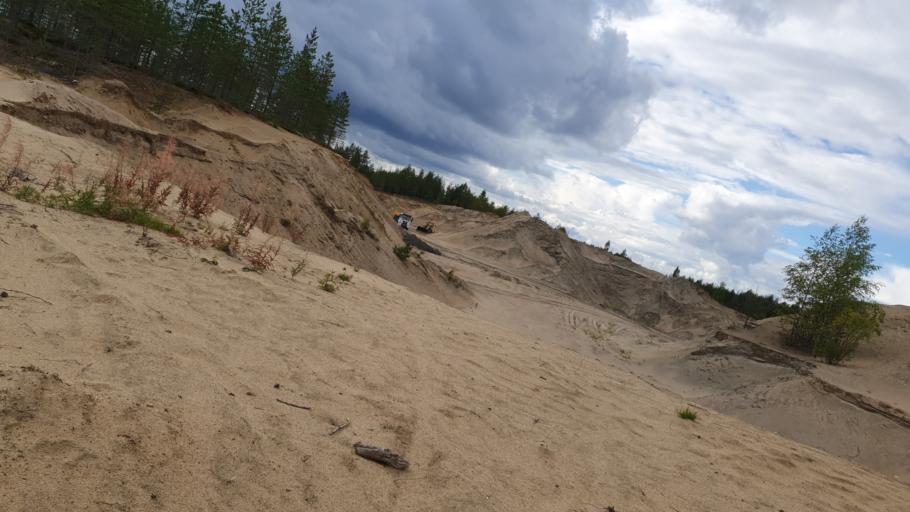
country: FI
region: Kainuu
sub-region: Kehys-Kainuu
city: Kuhmo
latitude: 64.1497
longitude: 29.3670
